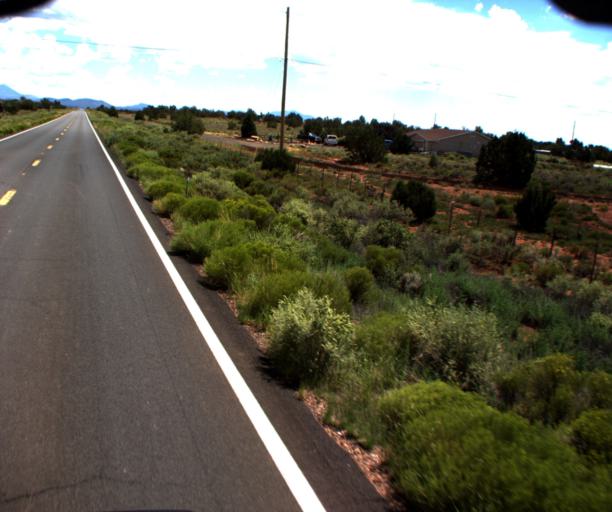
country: US
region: Arizona
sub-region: Coconino County
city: Williams
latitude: 35.6458
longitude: -112.1319
